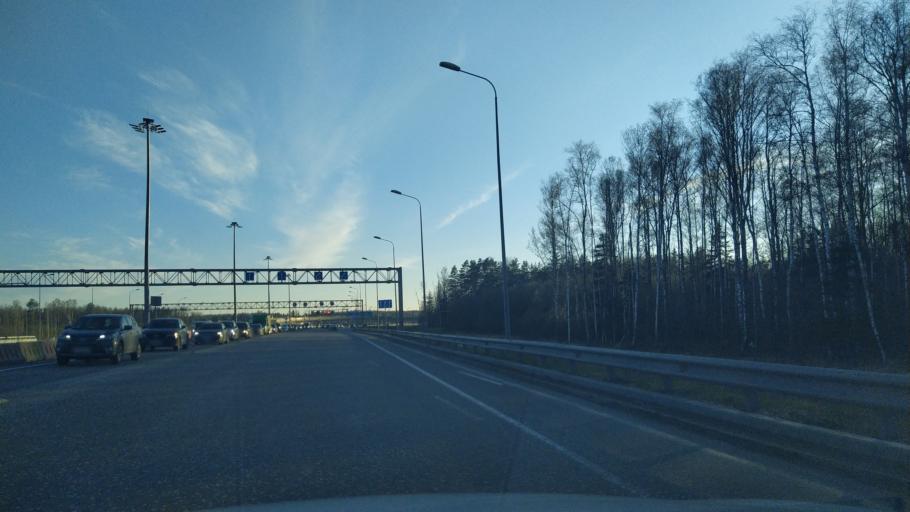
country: RU
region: St.-Petersburg
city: Pesochnyy
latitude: 60.0632
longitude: 30.1611
